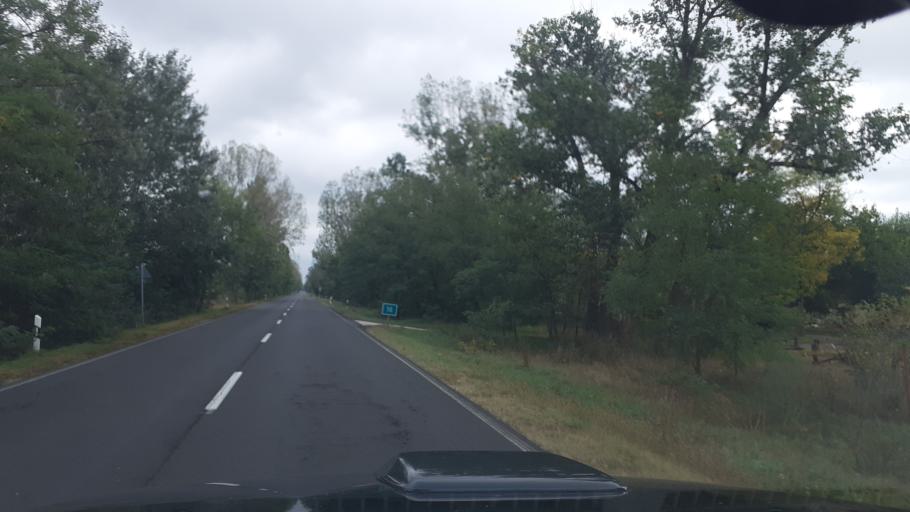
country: HU
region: Bacs-Kiskun
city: Agasegyhaza
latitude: 46.8767
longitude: 19.4808
